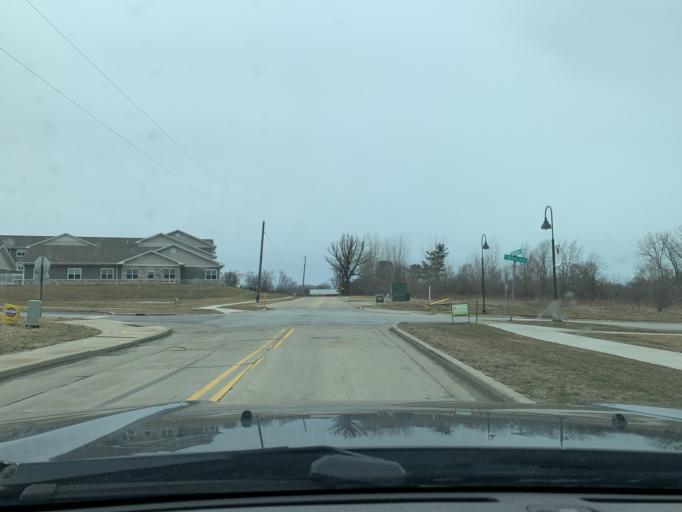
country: US
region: Indiana
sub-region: Porter County
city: Chesterton
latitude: 41.5864
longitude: -87.0408
